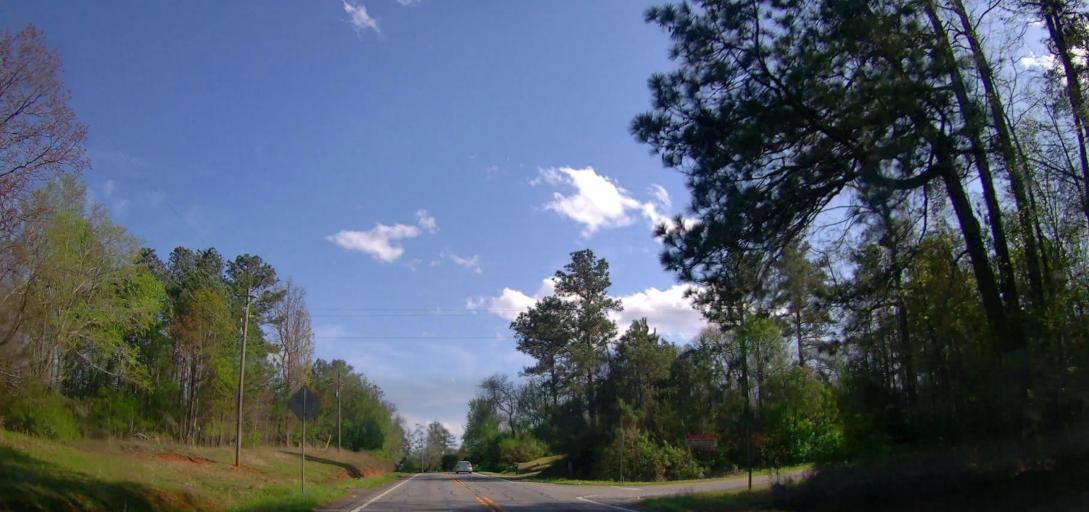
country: US
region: Georgia
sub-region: Baldwin County
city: Hardwick
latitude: 33.0852
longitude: -83.1711
